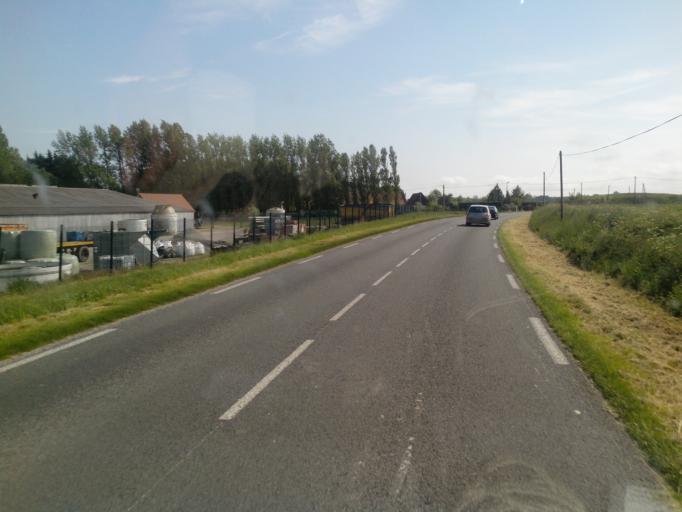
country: FR
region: Picardie
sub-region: Departement de la Somme
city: Quend
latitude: 50.3315
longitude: 1.6440
